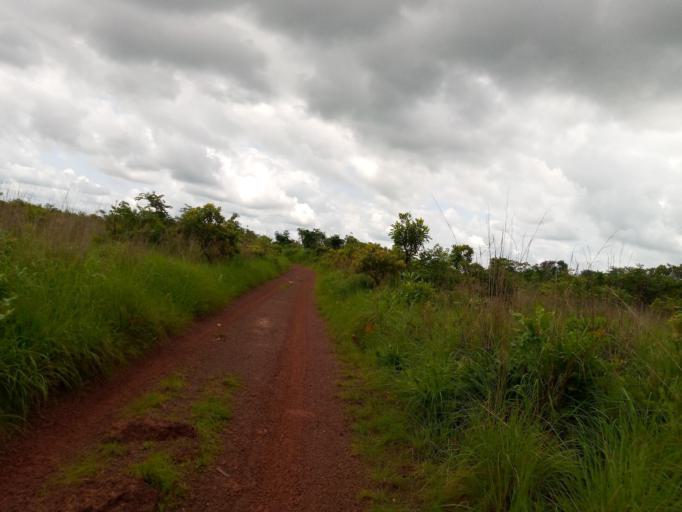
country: SL
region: Northern Province
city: Mange
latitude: 8.9842
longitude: -12.7286
